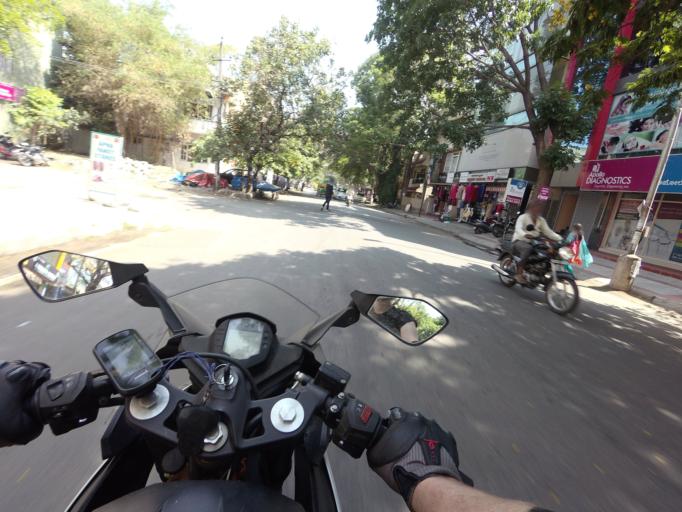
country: IN
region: Karnataka
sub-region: Bangalore Urban
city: Bangalore
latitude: 13.0030
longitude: 77.6609
